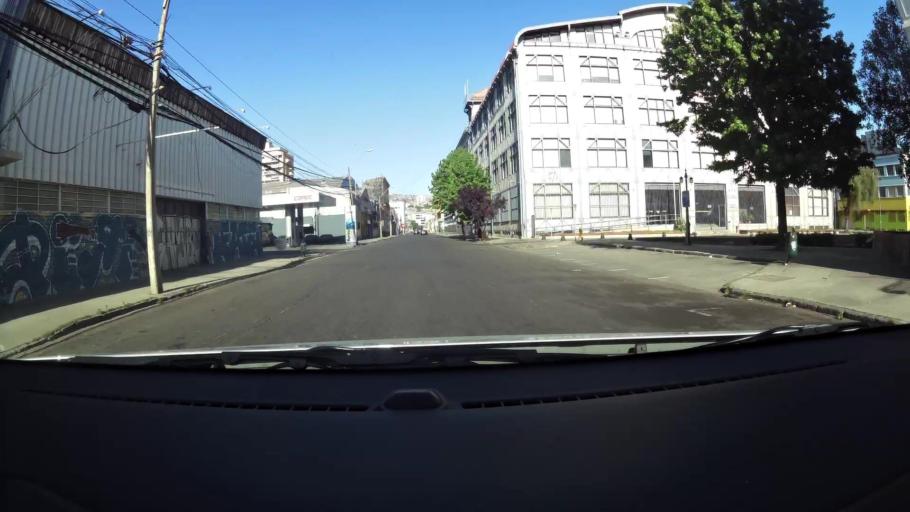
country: CL
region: Valparaiso
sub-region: Provincia de Valparaiso
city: Valparaiso
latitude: -33.0462
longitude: -71.6129
